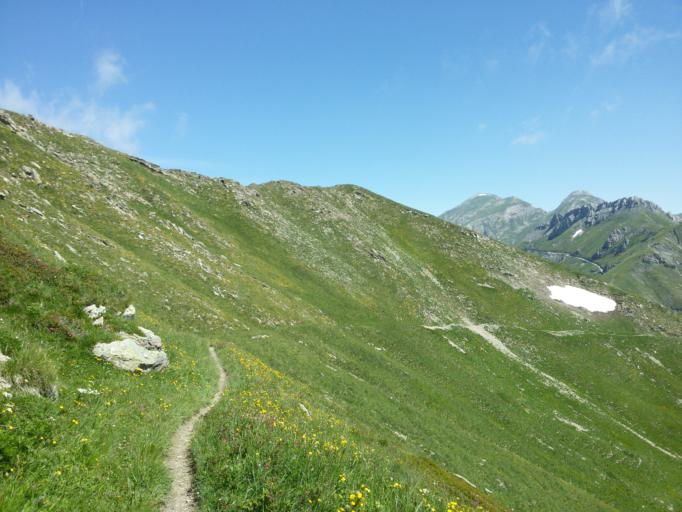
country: IT
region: Piedmont
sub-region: Provincia di Cuneo
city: Limone Piemonte
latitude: 44.1499
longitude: 7.6220
